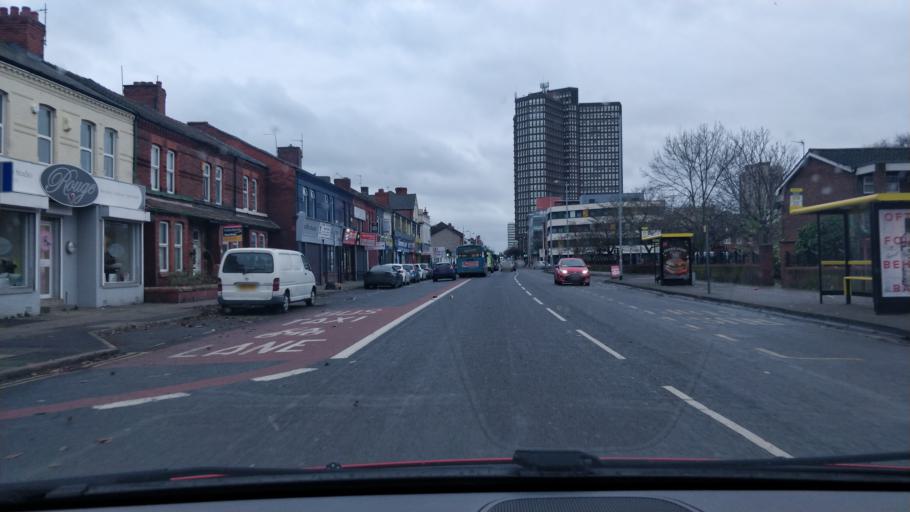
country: GB
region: England
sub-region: Sefton
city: Litherland
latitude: 53.4557
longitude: -2.9917
